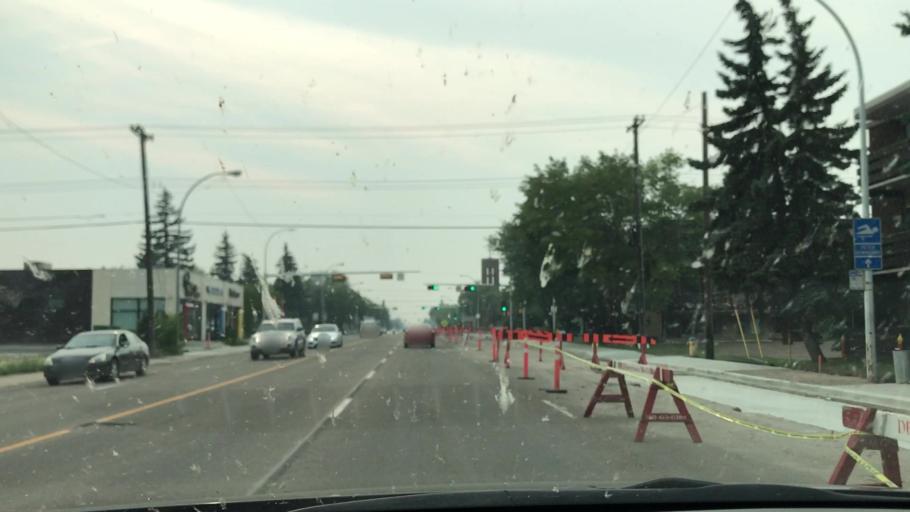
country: CA
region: Alberta
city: Edmonton
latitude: 53.5589
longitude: -113.5397
